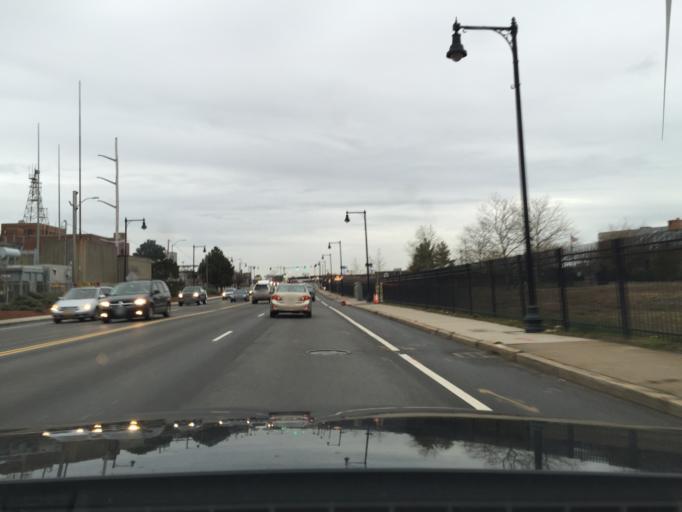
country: US
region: Massachusetts
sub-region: Middlesex County
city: Everett
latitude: 42.3922
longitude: -71.0693
